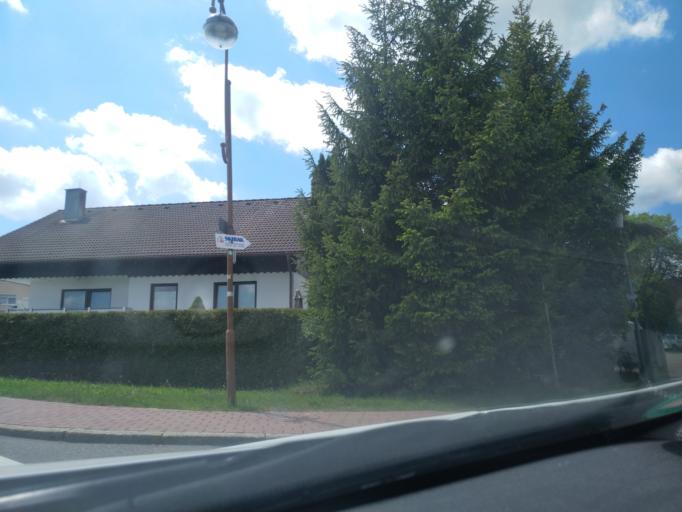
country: DE
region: Baden-Wuerttemberg
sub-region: Karlsruhe Region
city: Baiersbronn
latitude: 48.5937
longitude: 8.4156
